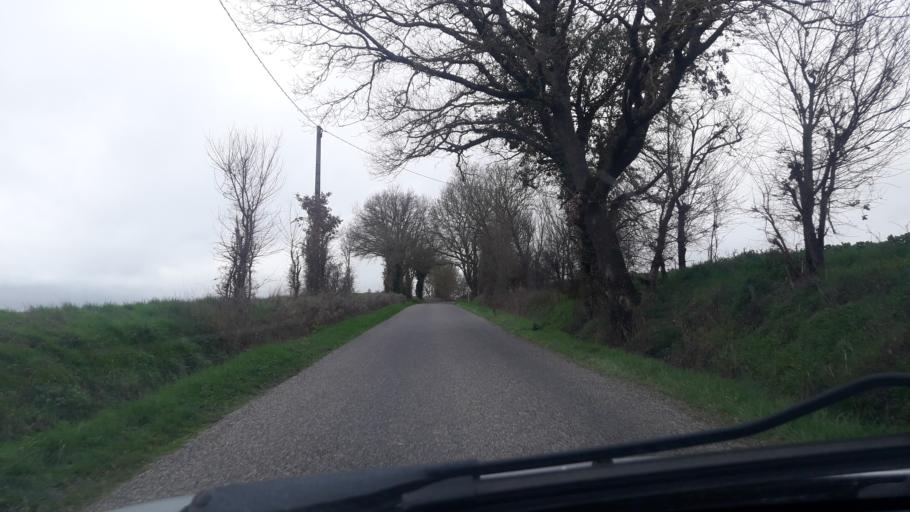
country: FR
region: Midi-Pyrenees
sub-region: Departement du Gers
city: Gimont
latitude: 43.6580
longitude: 0.9713
